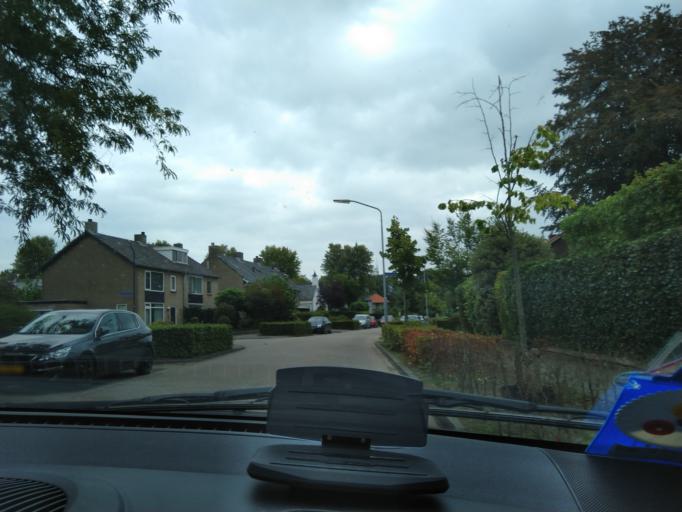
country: NL
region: North Brabant
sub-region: Gemeente Oosterhout
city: Oosterhout
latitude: 51.6392
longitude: 4.8535
